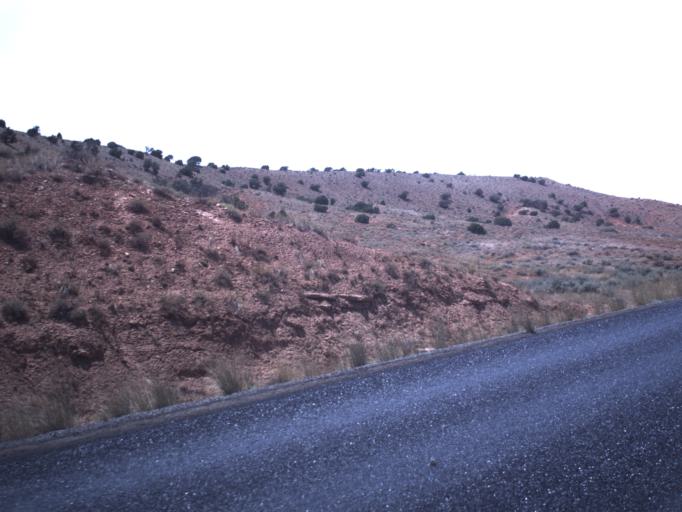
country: US
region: Utah
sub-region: Uintah County
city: Maeser
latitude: 40.4100
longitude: -109.7088
